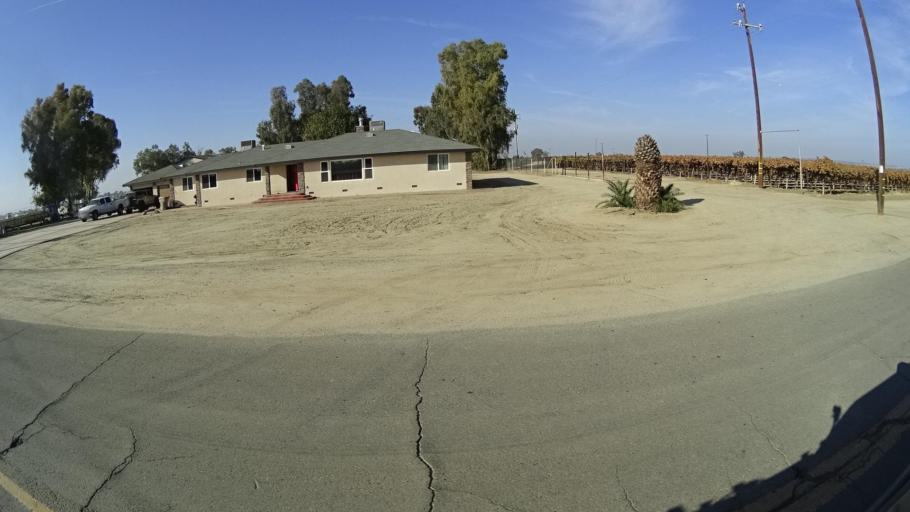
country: US
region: California
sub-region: Kern County
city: Lamont
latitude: 35.3480
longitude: -118.8965
